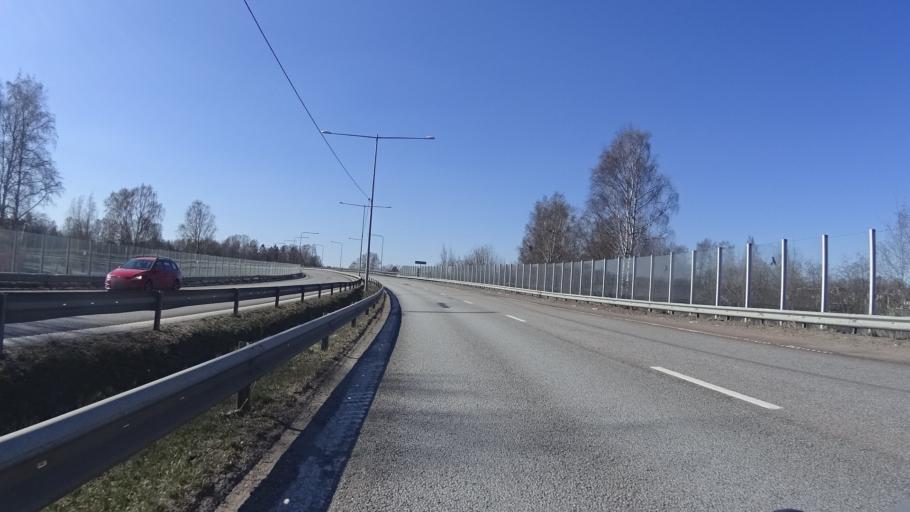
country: SE
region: Vaermland
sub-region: Karlstads Kommun
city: Karlstad
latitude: 59.3976
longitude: 13.5096
